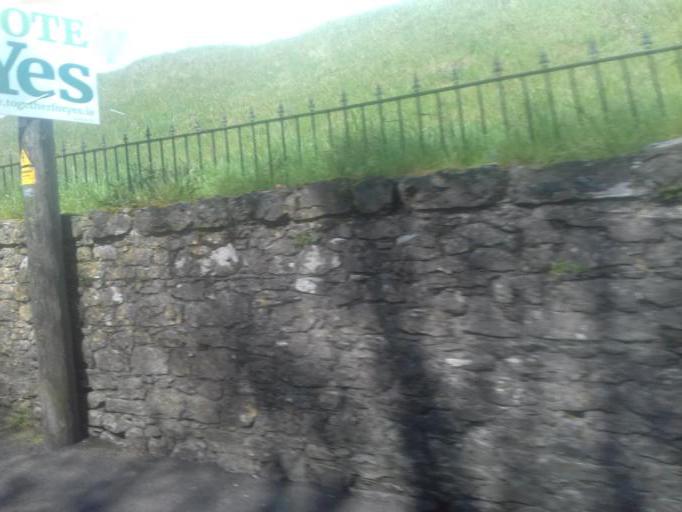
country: IE
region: Leinster
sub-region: Laois
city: Portlaoise
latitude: 53.0359
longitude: -7.2949
